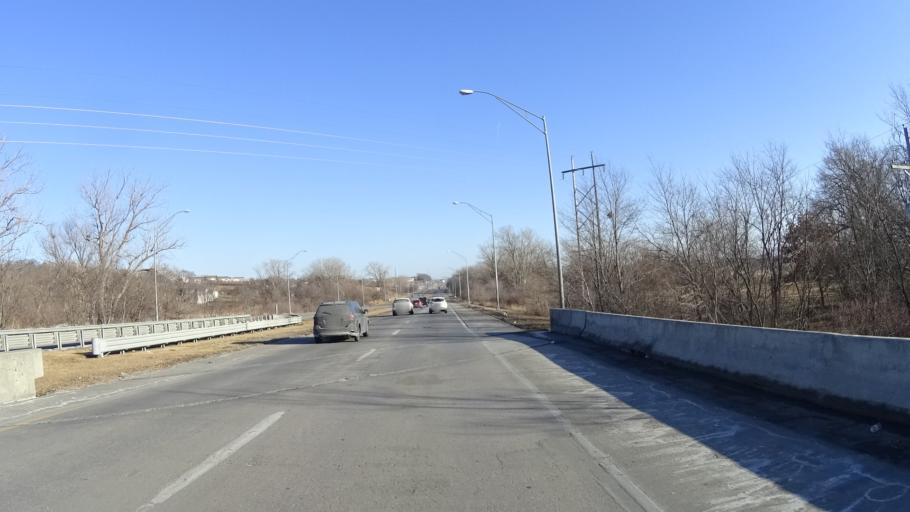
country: US
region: Nebraska
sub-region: Douglas County
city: Bennington
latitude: 41.2911
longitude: -96.0969
